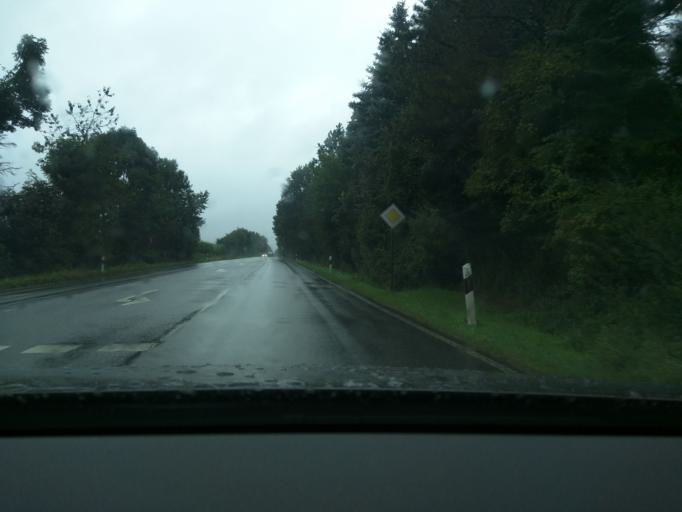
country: DE
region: Schleswig-Holstein
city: Wangelau
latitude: 53.4548
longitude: 10.5511
